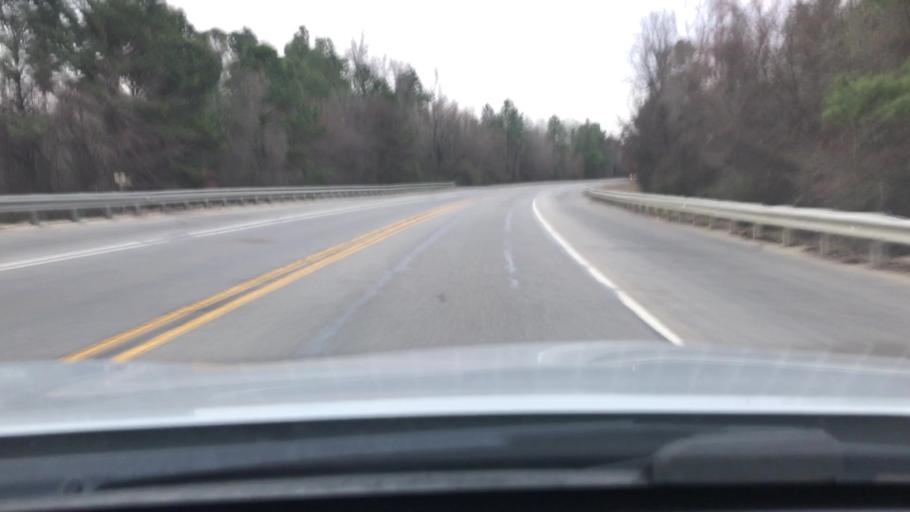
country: US
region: Arkansas
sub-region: Hempstead County
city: Hope
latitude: 33.6830
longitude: -93.5758
